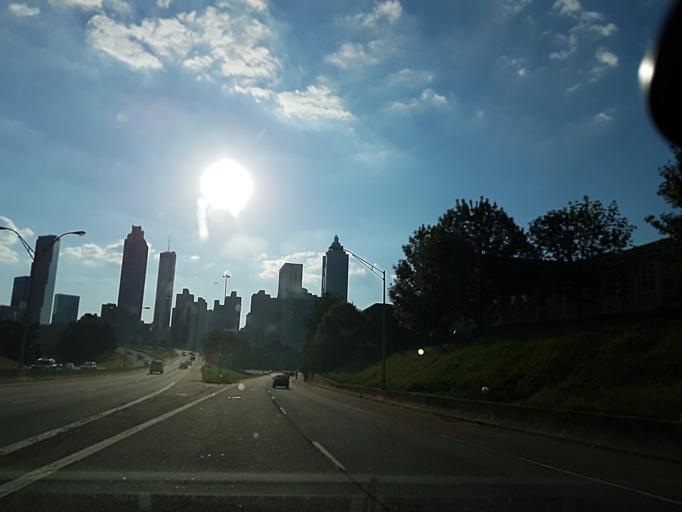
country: US
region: Georgia
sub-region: Fulton County
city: Atlanta
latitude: 33.7603
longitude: -84.3746
